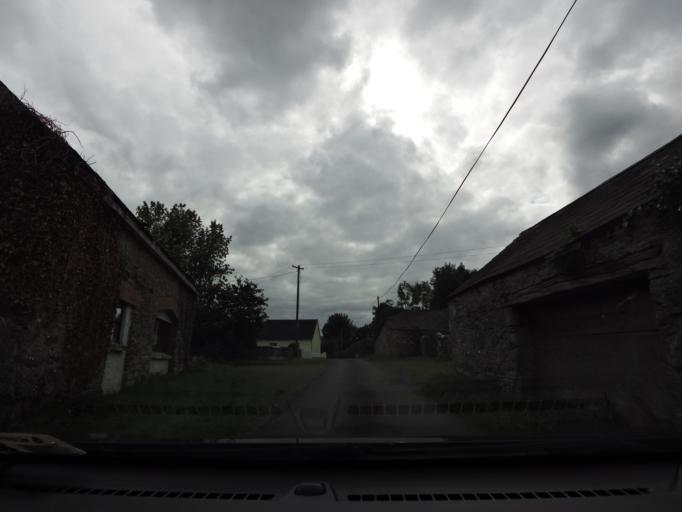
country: IE
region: Connaught
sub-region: County Galway
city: Loughrea
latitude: 53.1593
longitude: -8.4702
